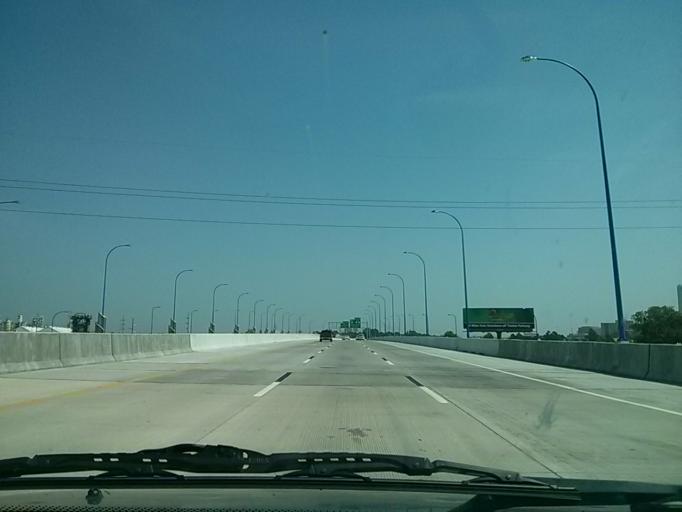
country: US
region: Oklahoma
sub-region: Tulsa County
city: Tulsa
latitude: 36.1369
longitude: -96.0078
